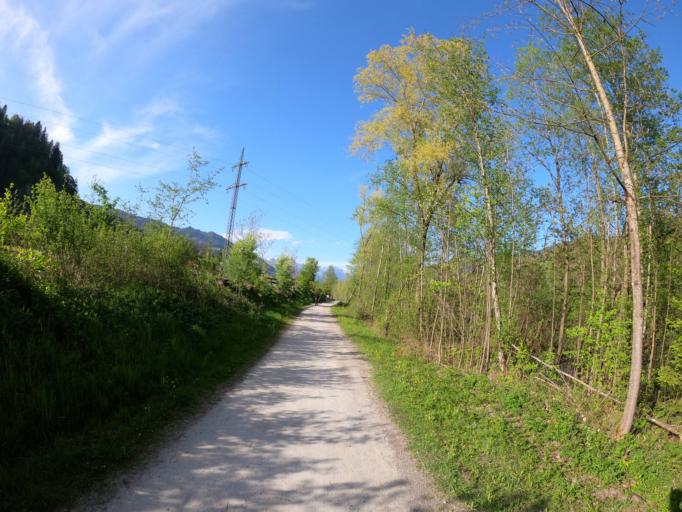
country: AT
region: Salzburg
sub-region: Politischer Bezirk Sankt Johann im Pongau
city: Sankt Johann im Pongau
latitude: 47.3290
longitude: 13.1881
